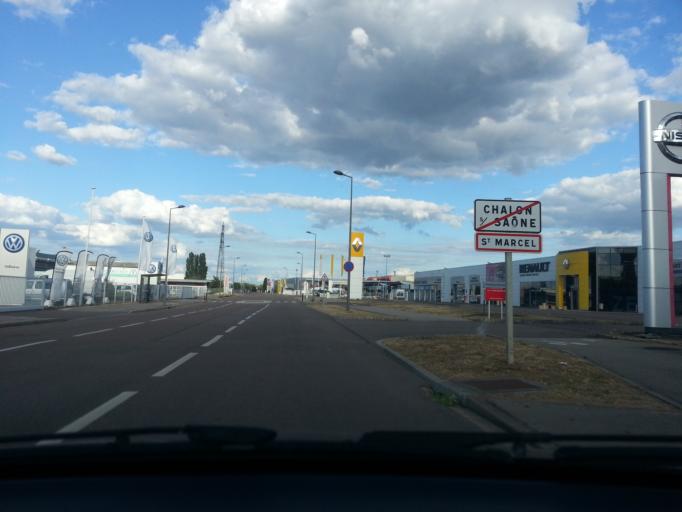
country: FR
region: Bourgogne
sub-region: Departement de Saone-et-Loire
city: Chalon-sur-Saone
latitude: 46.7686
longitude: 4.8635
